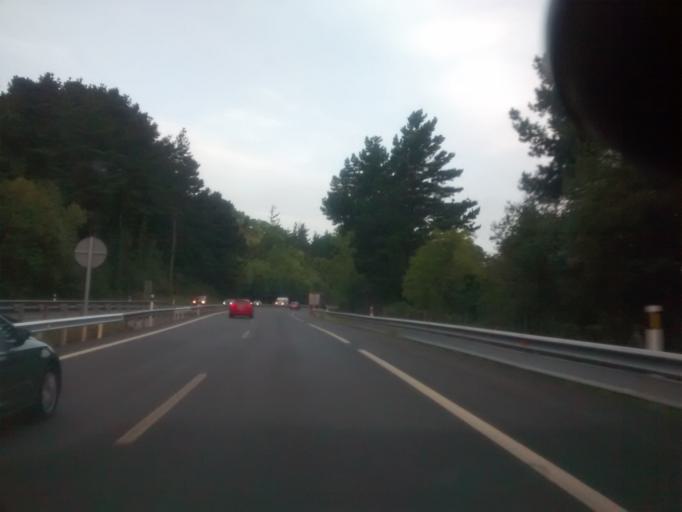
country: ES
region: Basque Country
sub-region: Provincia de Guipuzcoa
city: Deba
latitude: 43.2855
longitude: -2.3485
